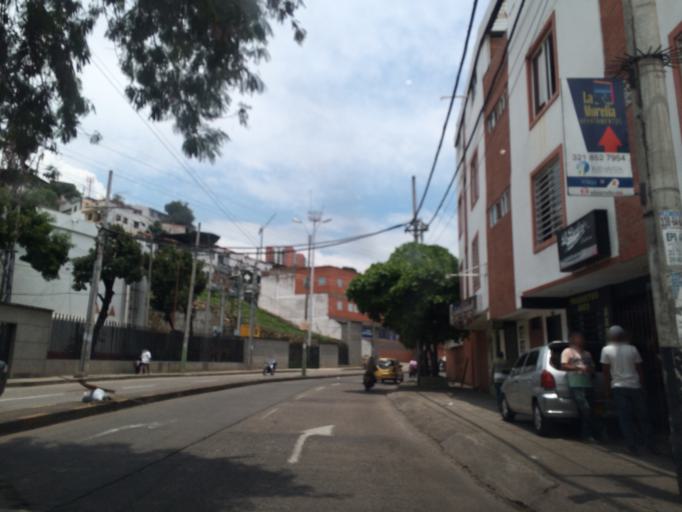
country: CO
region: Valle del Cauca
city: Cali
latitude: 3.4253
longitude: -76.5522
